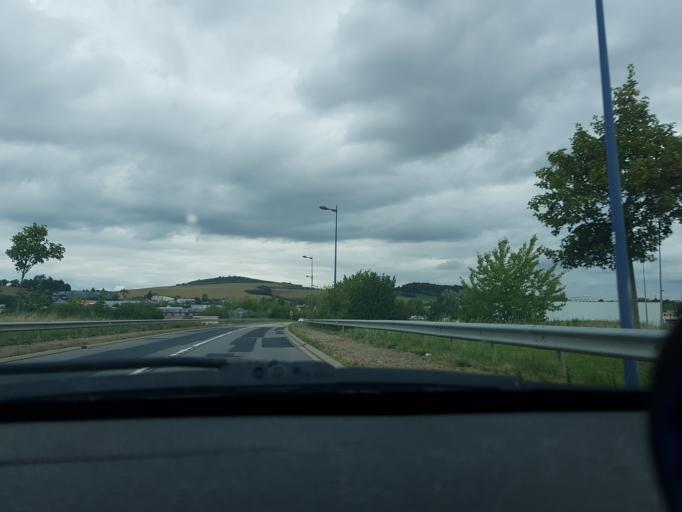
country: FR
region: Lorraine
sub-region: Departement de Meurthe-et-Moselle
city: Pulnoy
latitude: 48.7050
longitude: 6.2424
